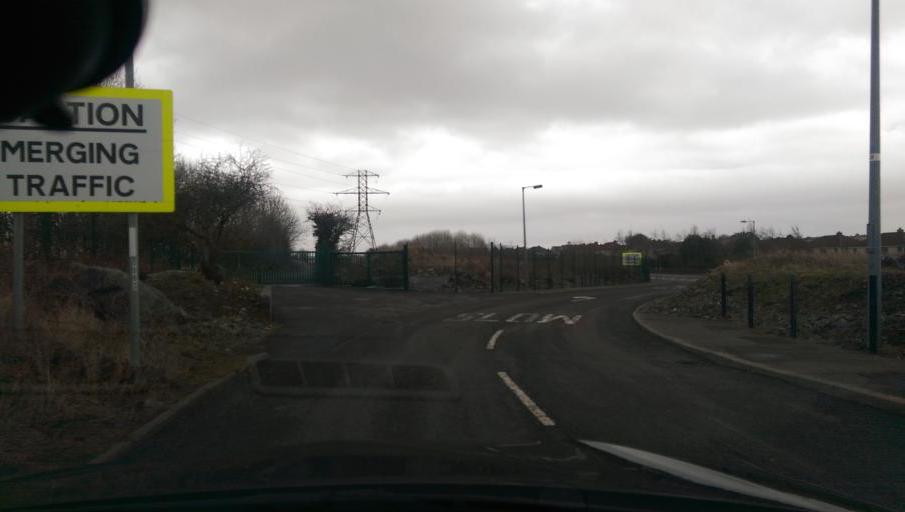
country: IE
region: Connaught
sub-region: County Galway
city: Gaillimh
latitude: 53.2915
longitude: -9.0009
